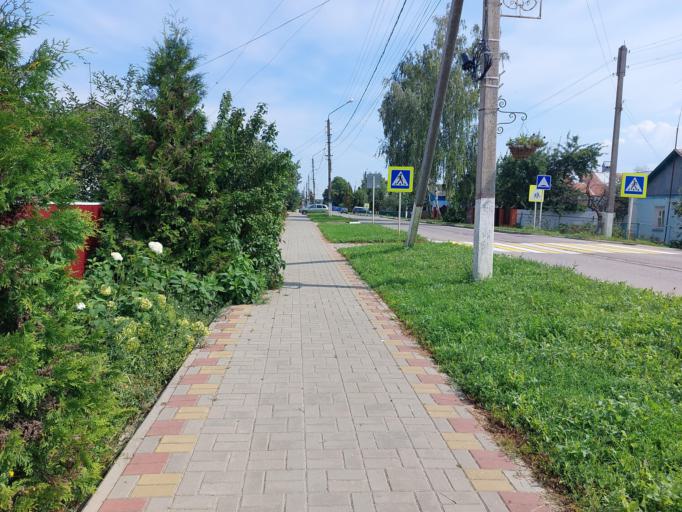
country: RU
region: Lipetsk
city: Dolgorukovo
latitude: 52.3237
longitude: 38.3581
